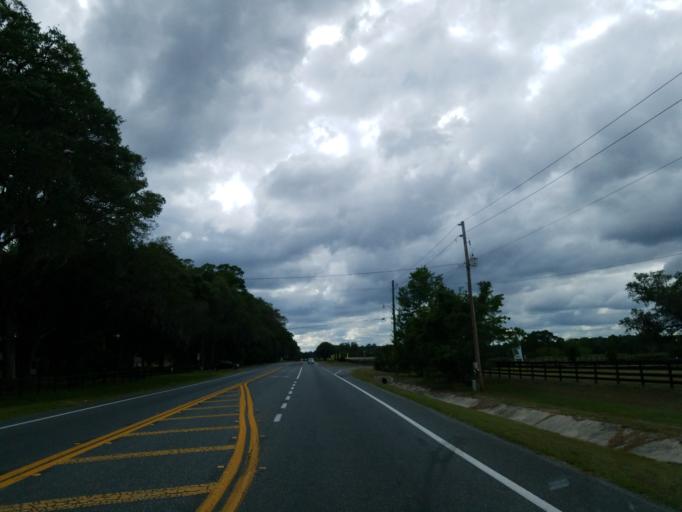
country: US
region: Florida
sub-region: Marion County
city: Ocala
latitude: 29.2595
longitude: -82.1022
